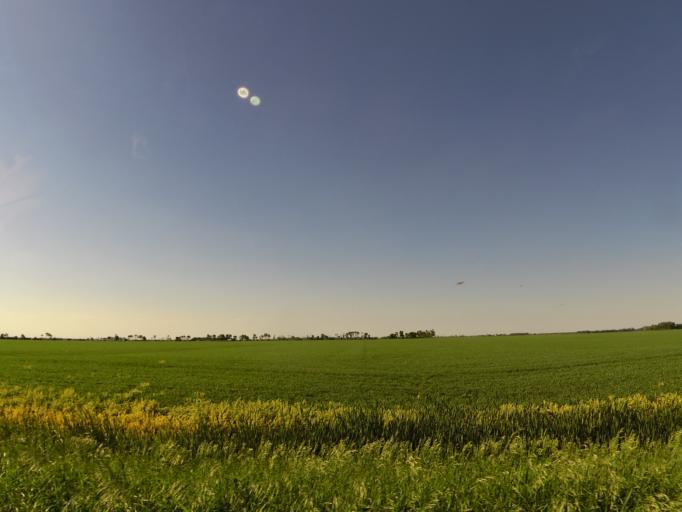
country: US
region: North Dakota
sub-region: Walsh County
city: Grafton
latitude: 48.3977
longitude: -97.2463
